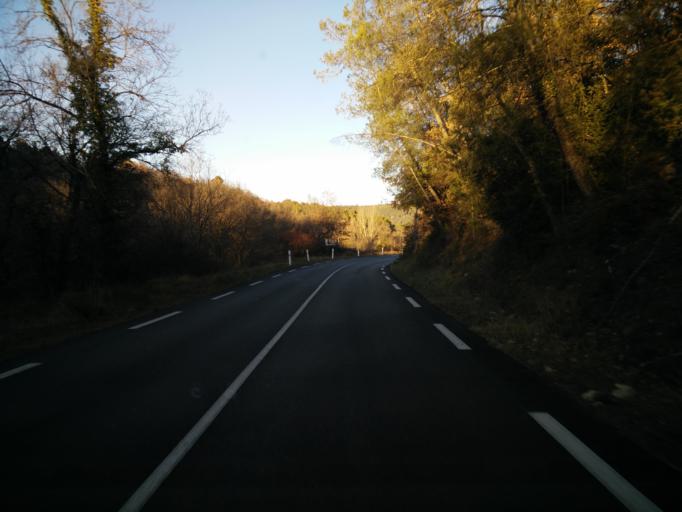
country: FR
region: Provence-Alpes-Cote d'Azur
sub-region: Departement du Var
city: Montferrat
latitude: 43.6001
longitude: 6.4745
